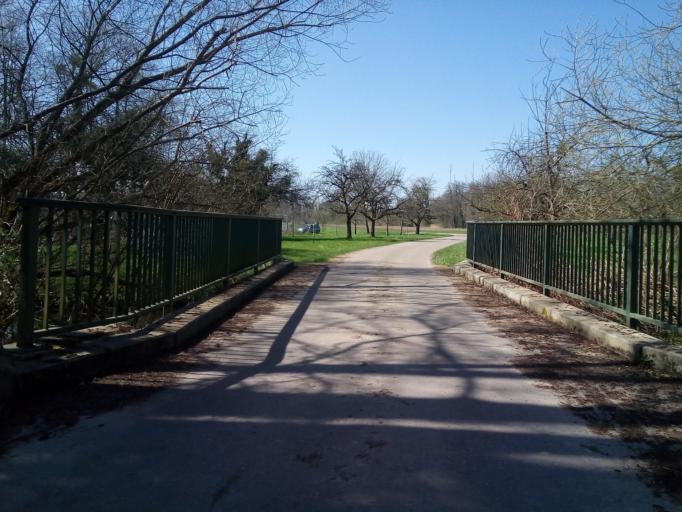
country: DE
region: Baden-Wuerttemberg
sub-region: Freiburg Region
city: Rheinau
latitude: 48.6576
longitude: 7.9129
